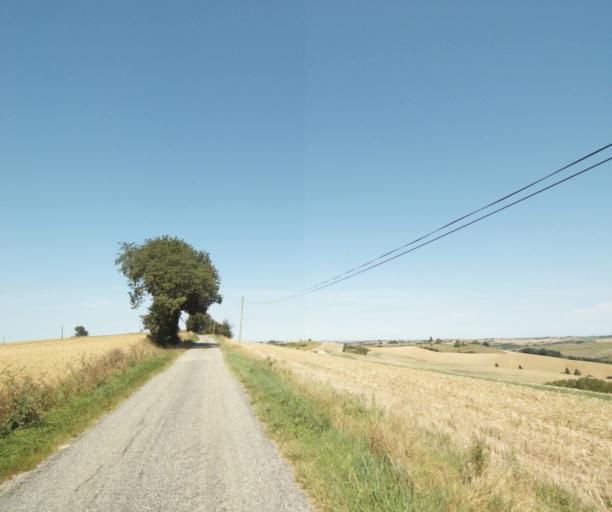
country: FR
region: Midi-Pyrenees
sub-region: Departement de l'Ariege
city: Lezat-sur-Leze
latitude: 43.2628
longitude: 1.3844
